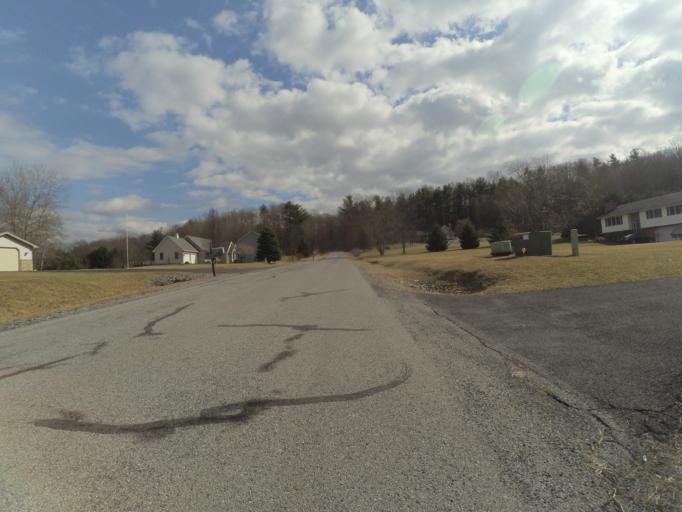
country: US
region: Pennsylvania
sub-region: Centre County
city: Stormstown
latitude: 40.7662
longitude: -78.0307
